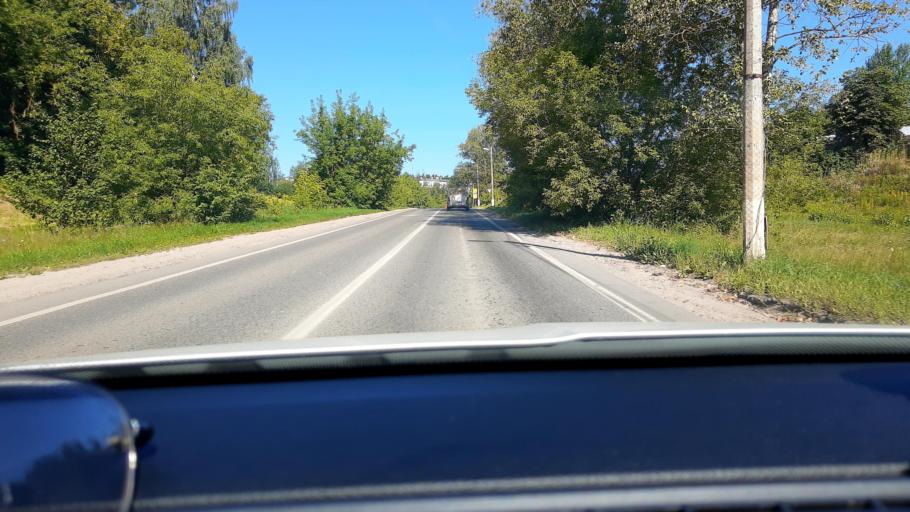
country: RU
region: Moskovskaya
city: Petrovo-Dal'neye
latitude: 55.7654
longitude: 37.2242
